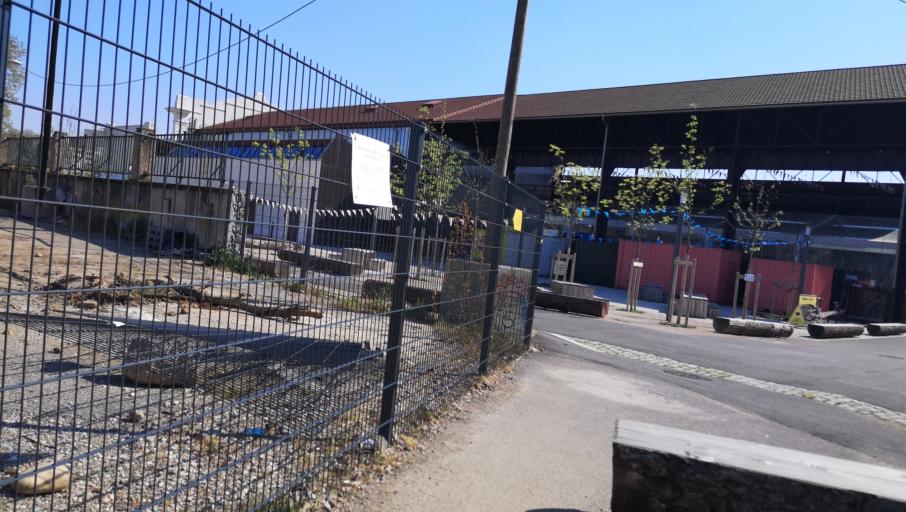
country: FR
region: Rhone-Alpes
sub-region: Departement du Rhone
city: La Mulatiere
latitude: 45.7379
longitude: 4.8197
